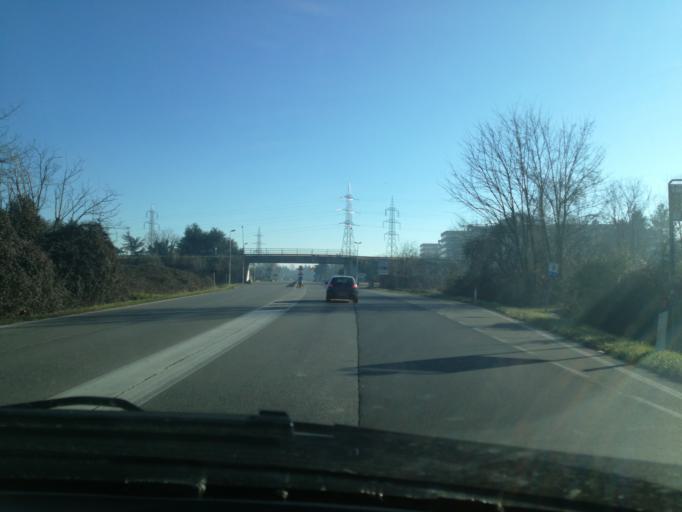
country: IT
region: Lombardy
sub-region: Provincia di Monza e Brianza
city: Concorezzo
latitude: 45.5763
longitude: 9.3342
